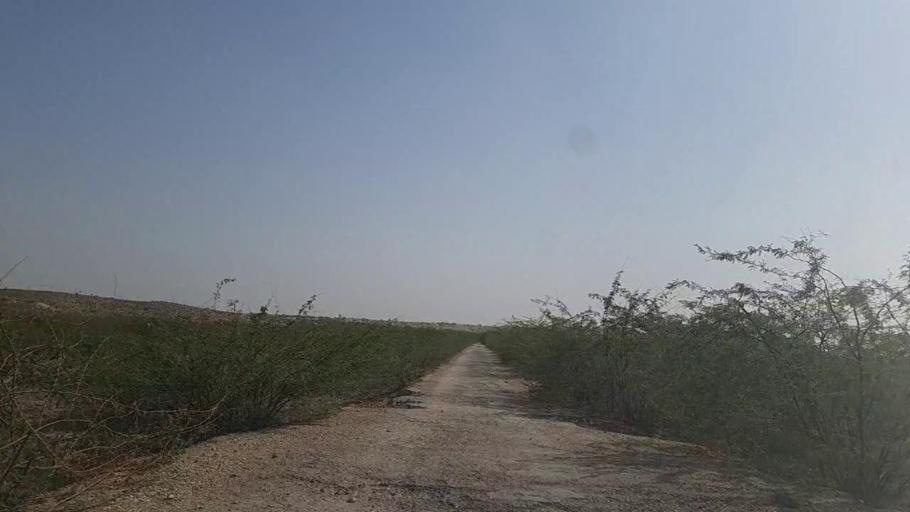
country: PK
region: Sindh
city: Naukot
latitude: 24.5806
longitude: 69.2934
